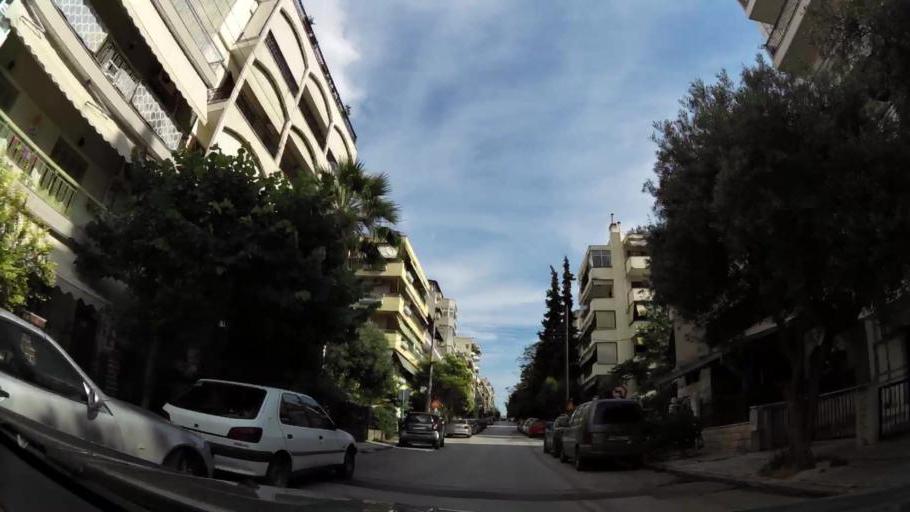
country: GR
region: Central Macedonia
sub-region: Nomos Thessalonikis
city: Kalamaria
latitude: 40.5825
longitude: 22.9568
